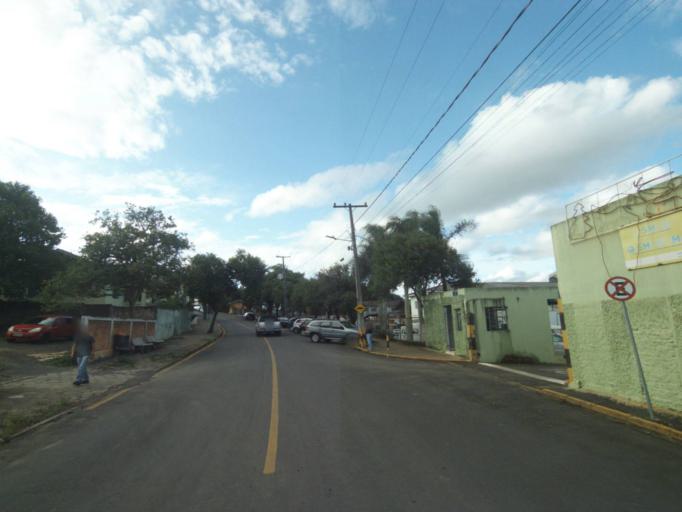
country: BR
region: Parana
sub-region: Telemaco Borba
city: Telemaco Borba
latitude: -24.3268
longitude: -50.6142
